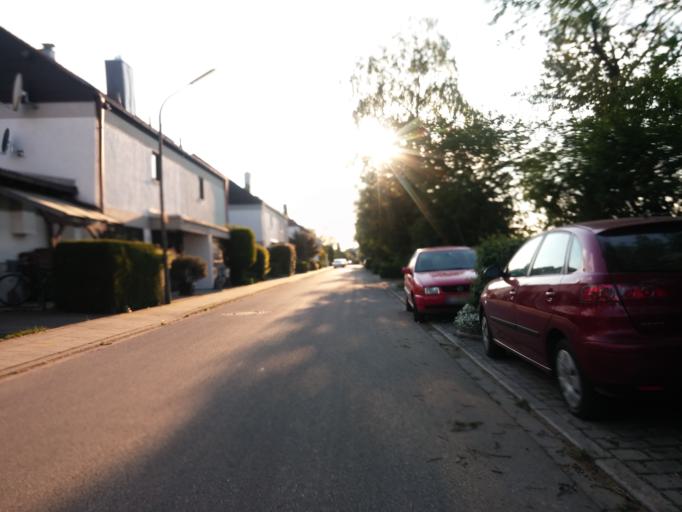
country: DE
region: Bavaria
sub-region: Upper Bavaria
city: Vaterstetten
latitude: 48.1065
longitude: 11.7947
